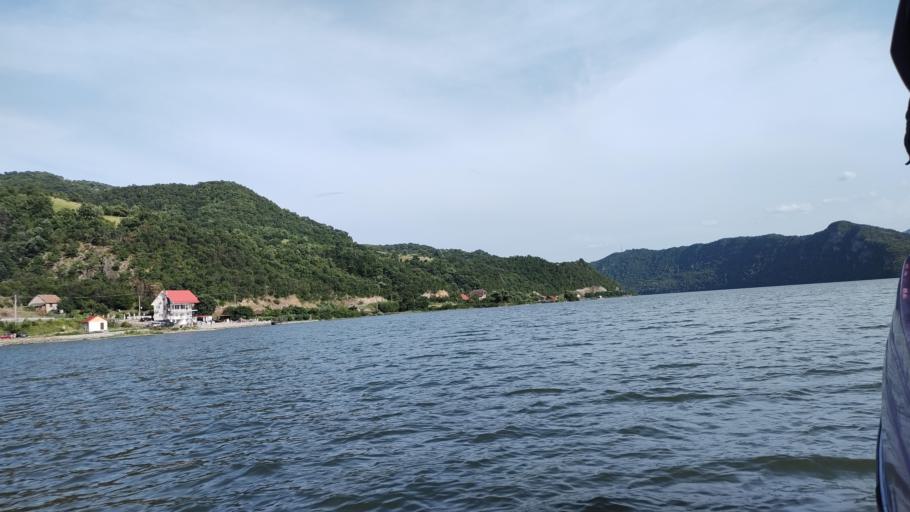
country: RO
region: Mehedinti
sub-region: Comuna Svinita
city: Svinita
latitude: 44.5611
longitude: 22.0311
